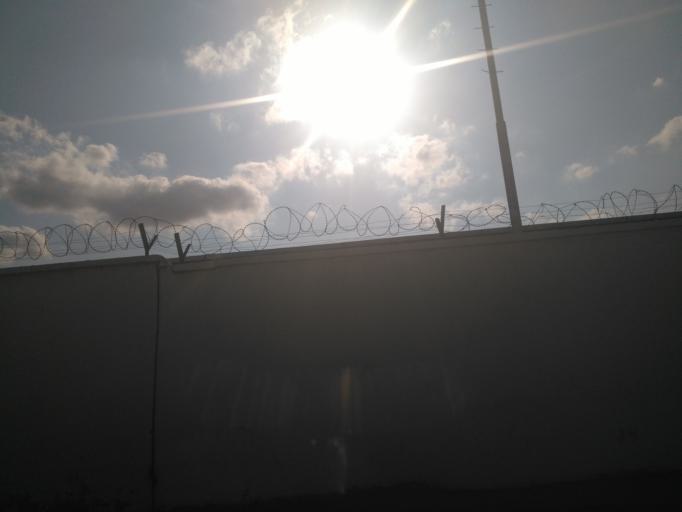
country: TZ
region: Pwani
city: Vikindu
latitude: -6.9209
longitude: 39.2659
